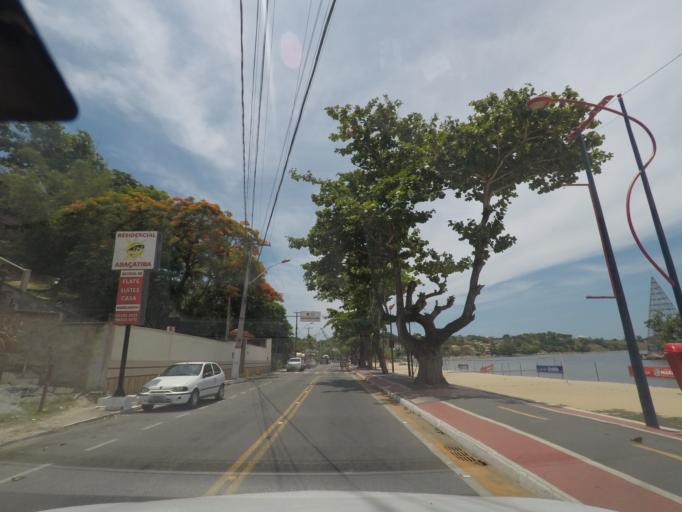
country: BR
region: Rio de Janeiro
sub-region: Marica
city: Marica
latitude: -22.9255
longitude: -42.8279
